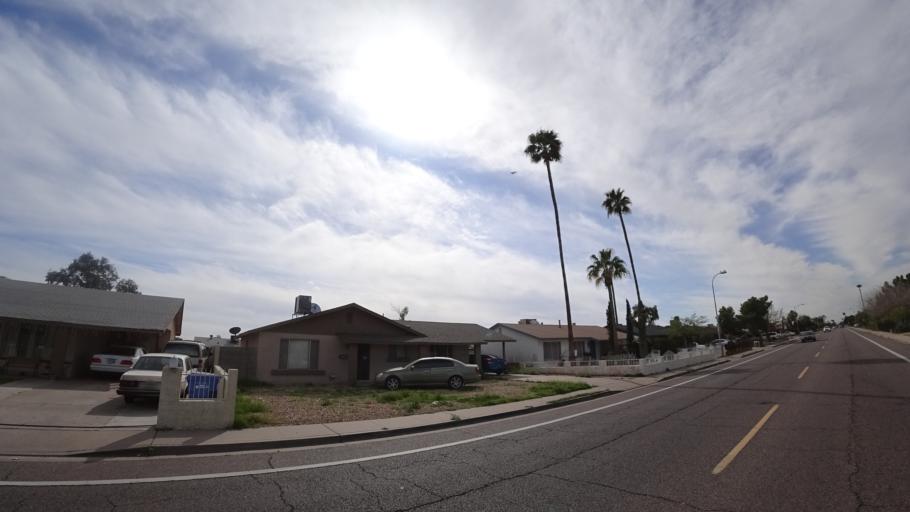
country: US
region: Arizona
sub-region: Maricopa County
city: Glendale
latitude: 33.4732
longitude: -112.1708
